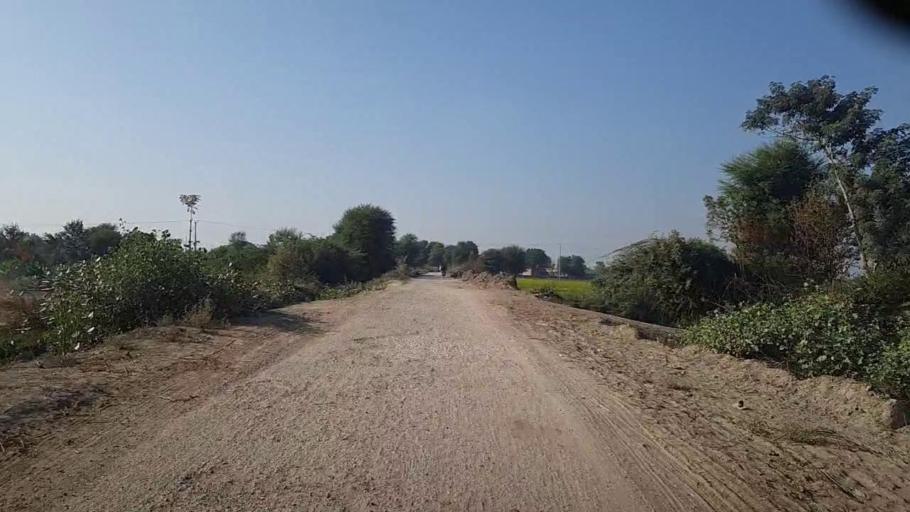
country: PK
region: Sindh
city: Darya Khan Marri
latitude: 26.6780
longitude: 68.3729
